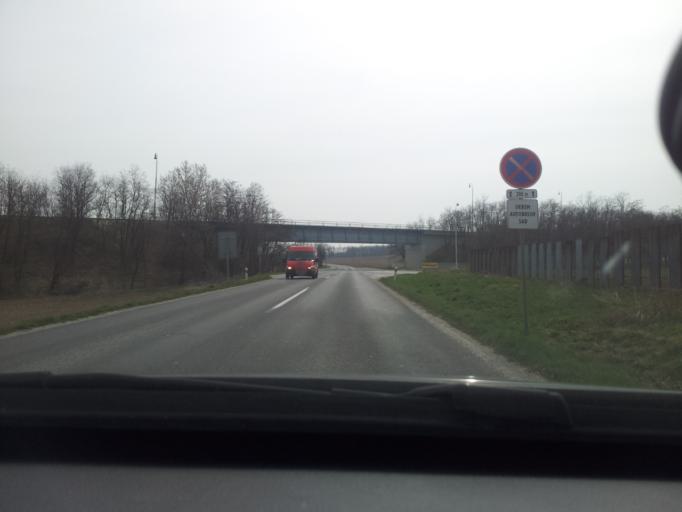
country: SK
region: Trnavsky
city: Hlohovec
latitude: 48.3832
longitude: 17.8701
